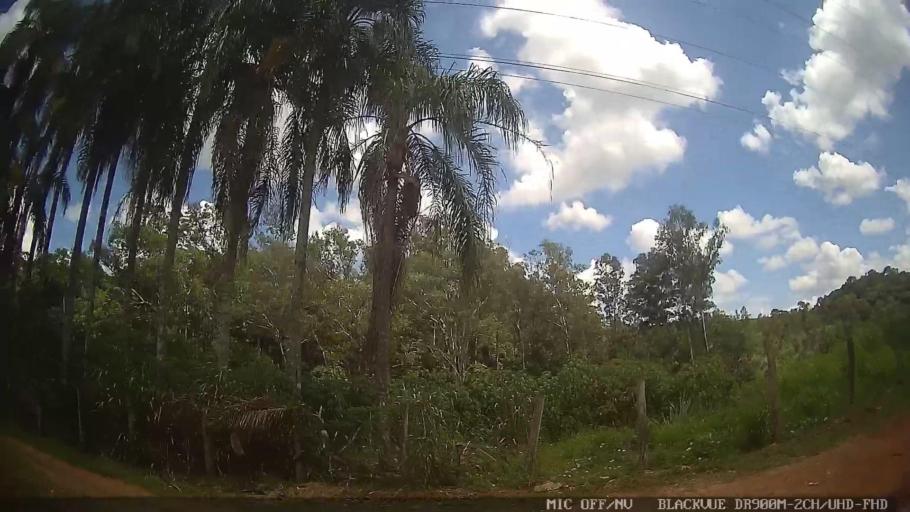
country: BR
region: Sao Paulo
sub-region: Atibaia
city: Atibaia
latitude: -23.1591
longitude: -46.6244
